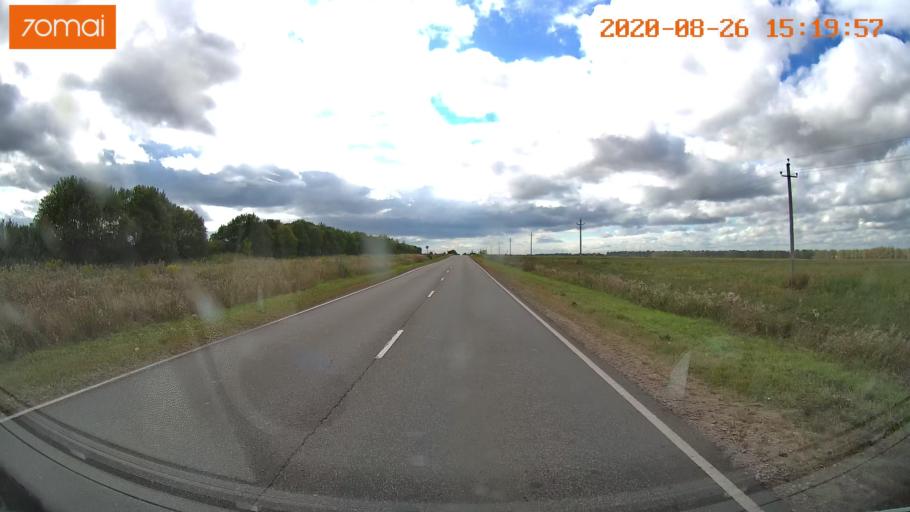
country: RU
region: Tula
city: Severo-Zadonsk
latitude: 54.1418
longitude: 38.5087
